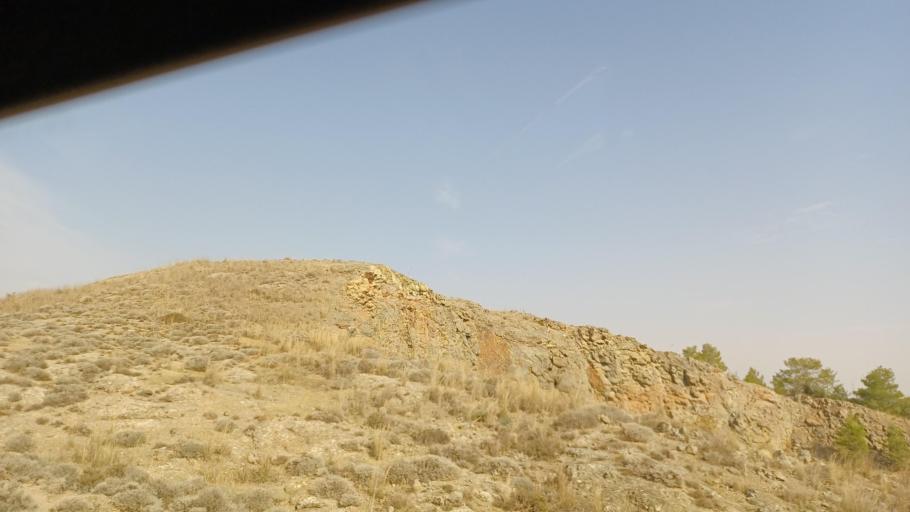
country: CY
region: Larnaka
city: Mosfiloti
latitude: 34.9689
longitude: 33.4254
